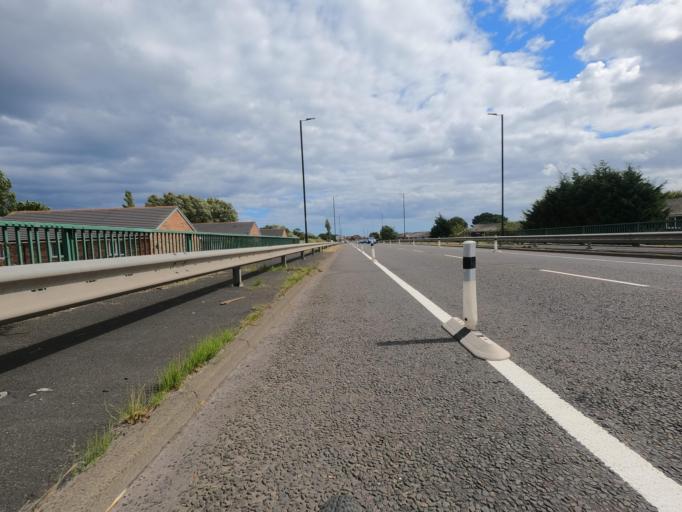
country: GB
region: England
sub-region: Borough of North Tyneside
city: Shiremoor
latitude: 55.0238
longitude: -1.4861
